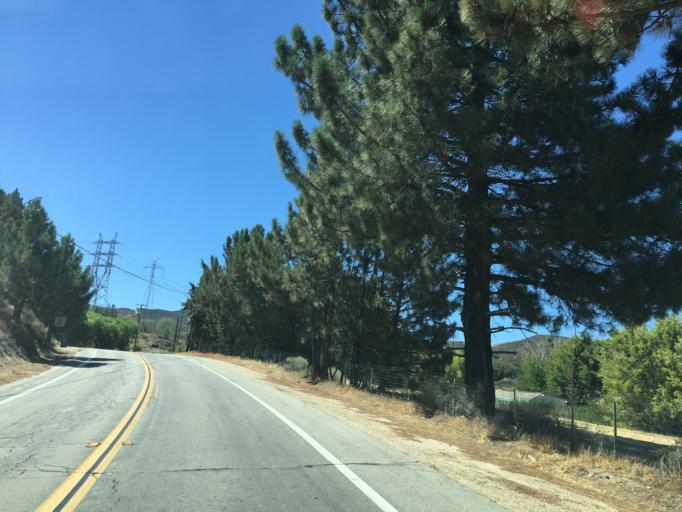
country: US
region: California
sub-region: Los Angeles County
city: Green Valley
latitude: 34.6529
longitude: -118.3772
